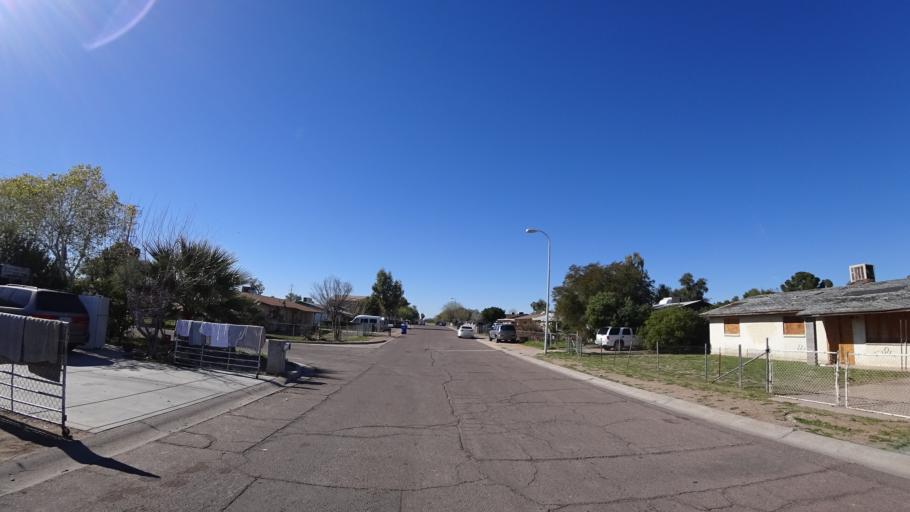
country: US
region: Arizona
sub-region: Maricopa County
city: Avondale
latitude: 33.4126
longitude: -112.3293
